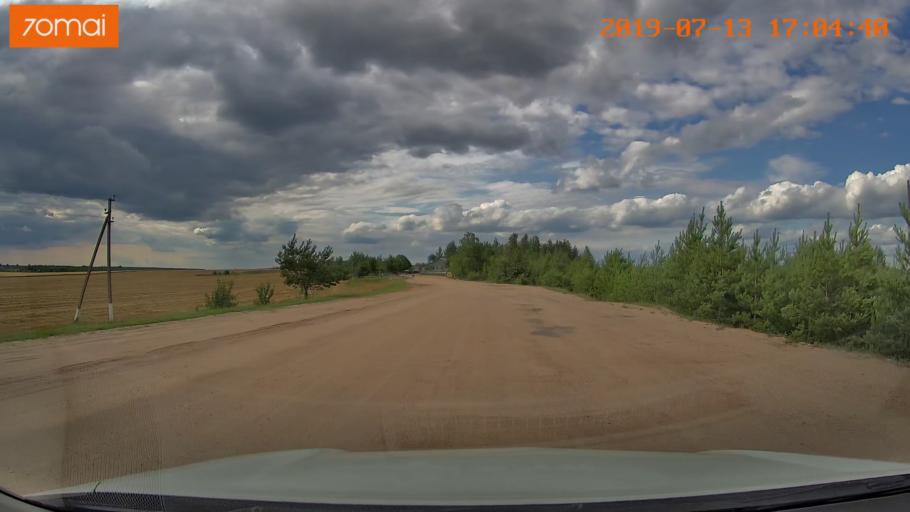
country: BY
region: Mogilev
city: Kirawsk
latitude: 53.2713
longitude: 29.3676
